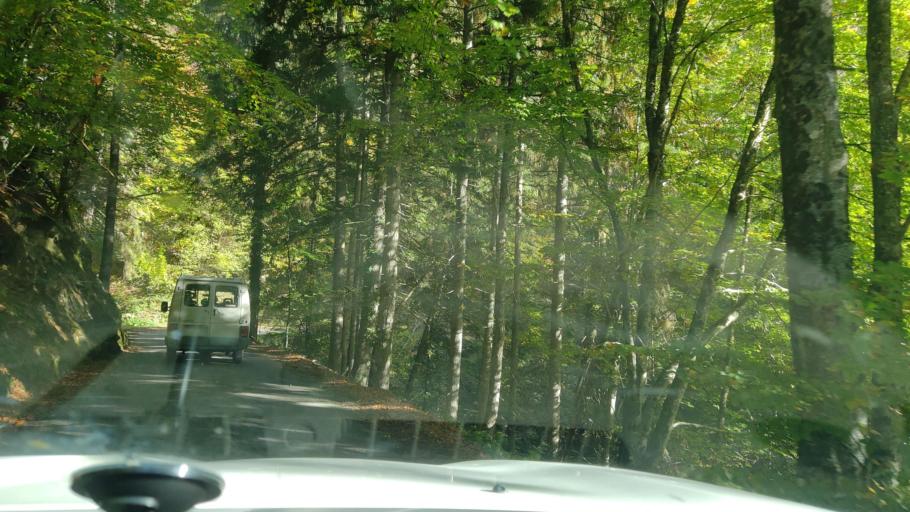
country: FR
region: Rhone-Alpes
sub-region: Departement de la Savoie
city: Beaufort
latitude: 45.7219
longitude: 6.4960
